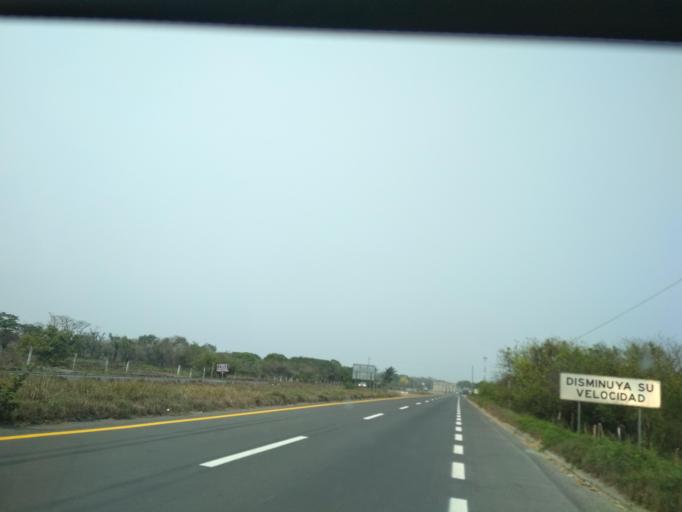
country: MX
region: Veracruz
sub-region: Veracruz
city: Delfino Victoria (Santa Fe)
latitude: 19.1986
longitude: -96.2721
